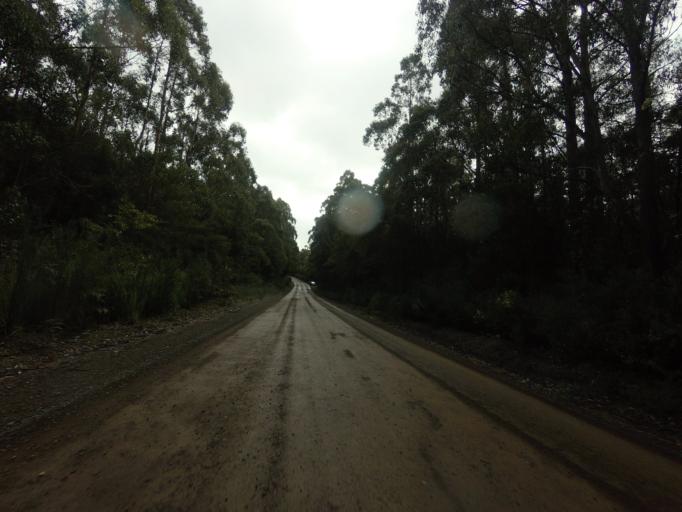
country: AU
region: Tasmania
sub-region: Huon Valley
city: Geeveston
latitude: -43.4663
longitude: 146.8995
